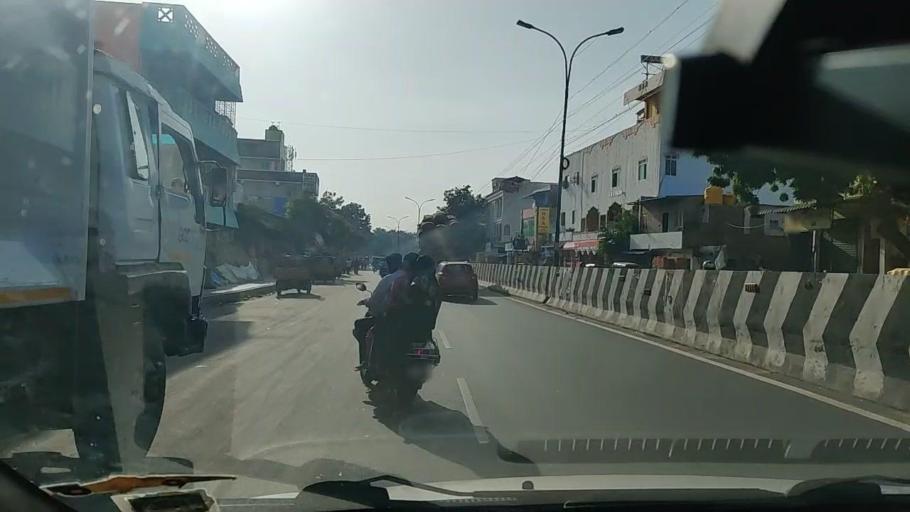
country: IN
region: Tamil Nadu
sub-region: Thiruvallur
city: Chinnasekkadu
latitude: 13.1220
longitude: 80.2515
